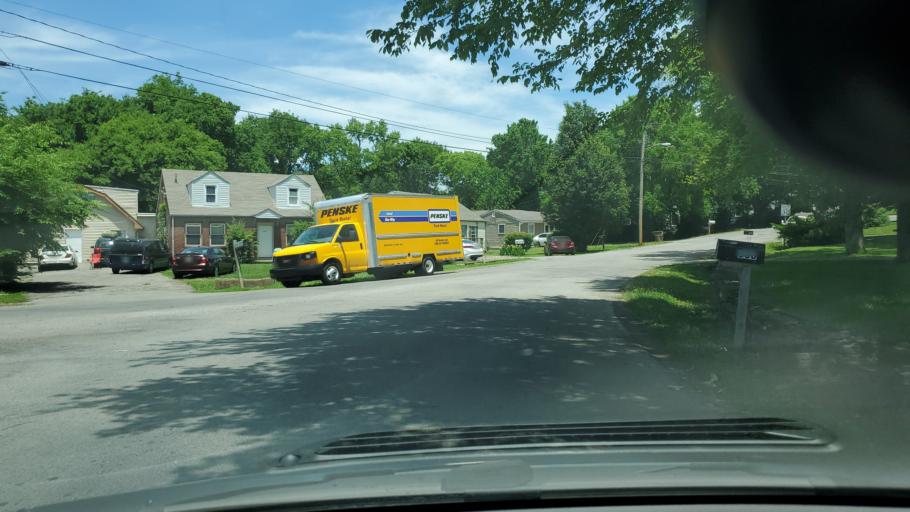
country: US
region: Tennessee
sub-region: Davidson County
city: Nashville
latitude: 36.2060
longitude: -86.7574
